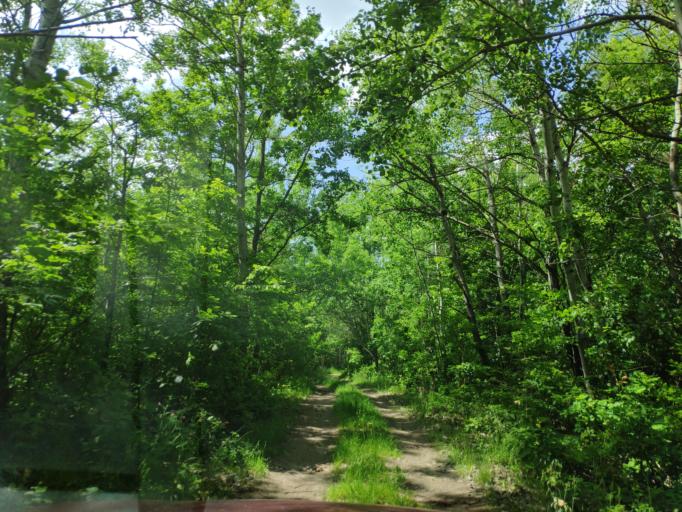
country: SK
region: Kosicky
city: Medzev
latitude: 48.7204
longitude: 20.9620
